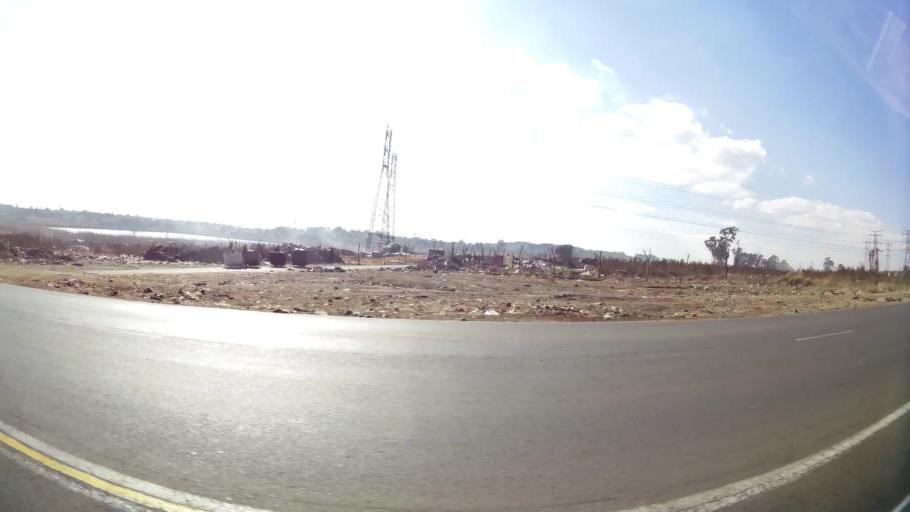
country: ZA
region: Gauteng
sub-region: City of Johannesburg Metropolitan Municipality
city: Soweto
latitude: -26.2827
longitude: 27.9168
